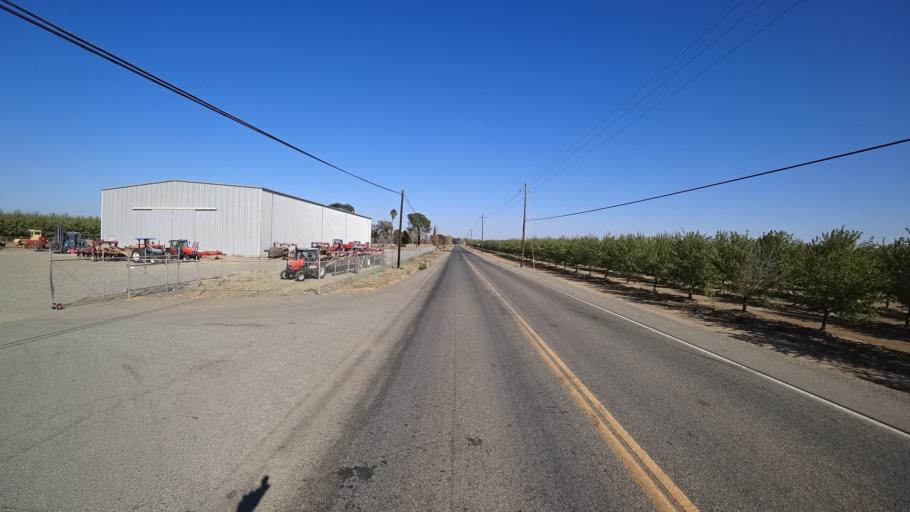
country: US
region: California
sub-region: Yolo County
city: Cottonwood
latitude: 38.6627
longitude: -121.9709
